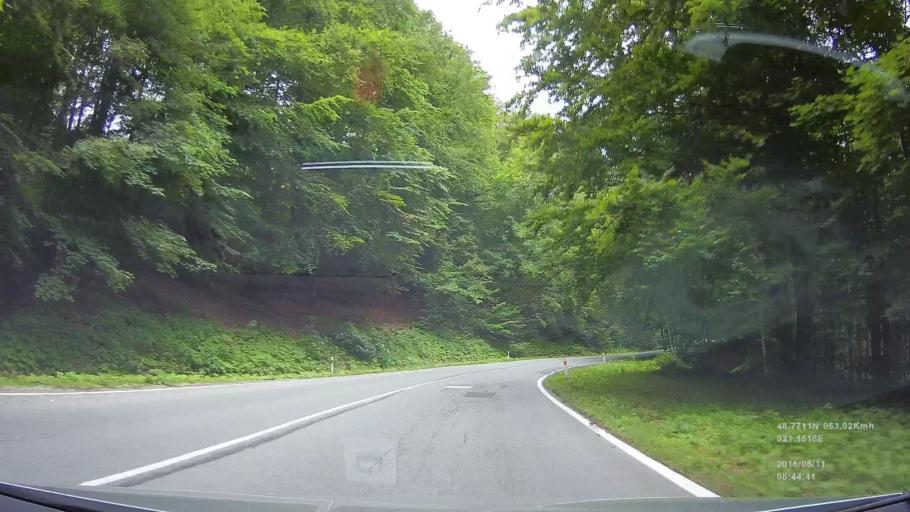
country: SK
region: Kosicky
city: Kosice
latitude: 48.7534
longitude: 21.1984
